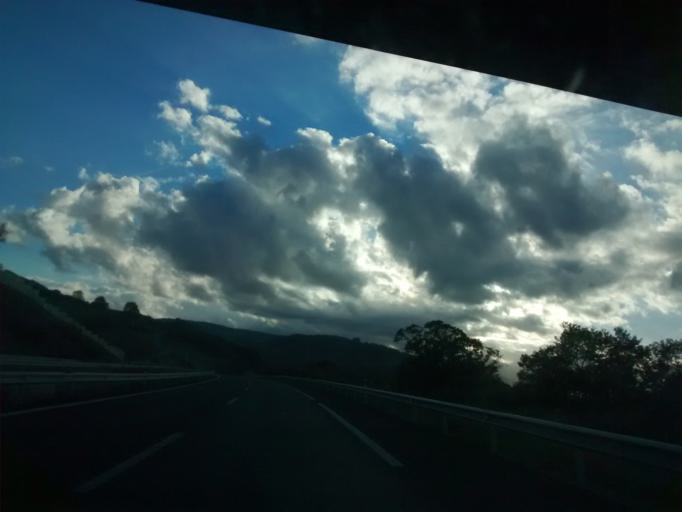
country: ES
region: Cantabria
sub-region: Provincia de Cantabria
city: Penagos
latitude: 43.3485
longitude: -3.7839
